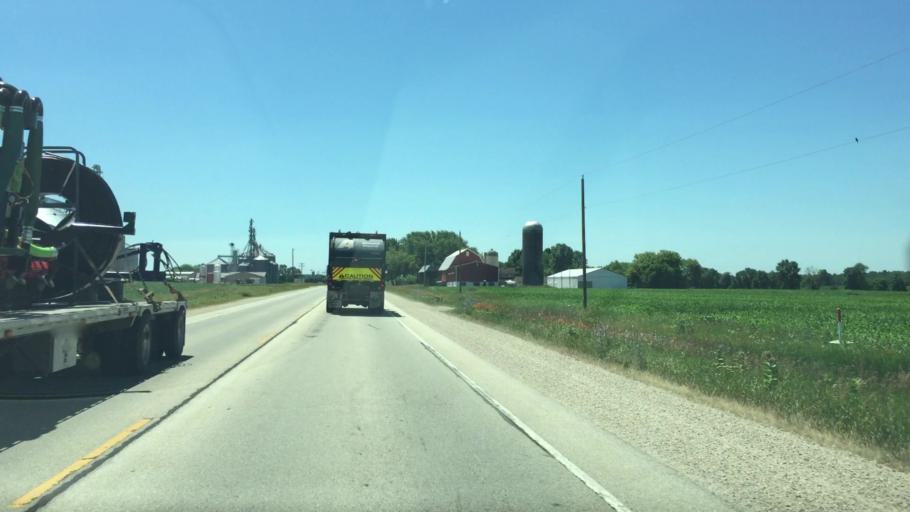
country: US
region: Wisconsin
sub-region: Calumet County
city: Chilton
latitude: 44.0791
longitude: -88.1635
